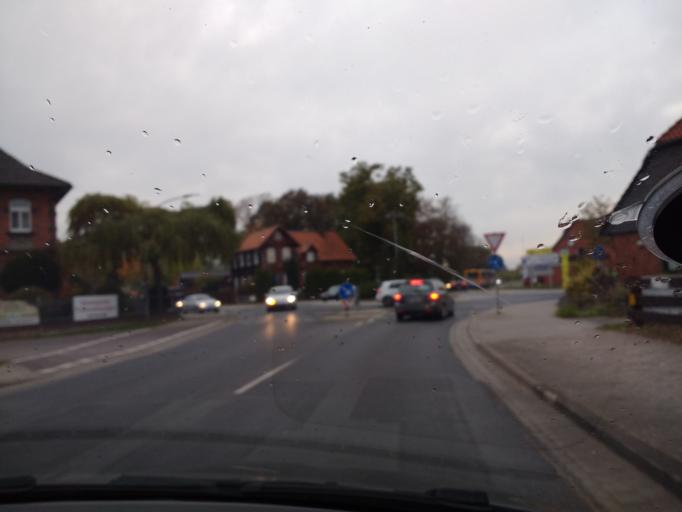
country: DE
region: Lower Saxony
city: Isenbuttel
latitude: 52.4358
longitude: 10.5719
